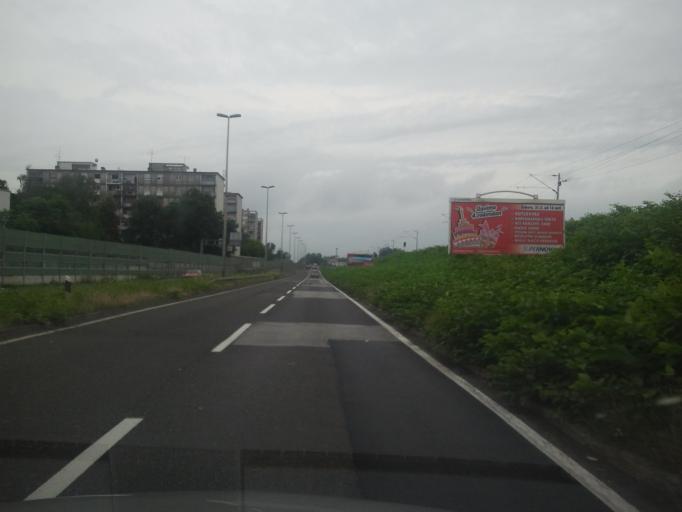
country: HR
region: Karlovacka
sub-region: Grad Karlovac
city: Karlovac
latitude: 45.4861
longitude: 15.5516
